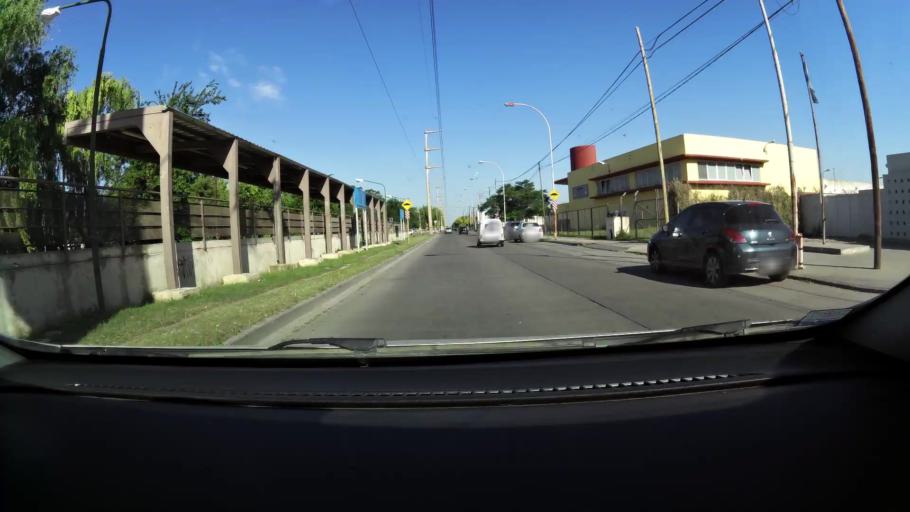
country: AR
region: Cordoba
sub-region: Departamento de Capital
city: Cordoba
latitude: -31.3693
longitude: -64.2115
